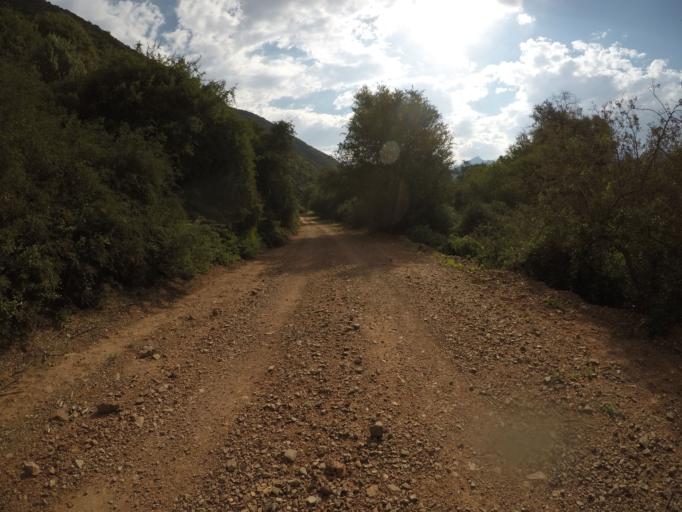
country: ZA
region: Eastern Cape
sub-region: Cacadu District Municipality
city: Kareedouw
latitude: -33.6392
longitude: 24.3041
